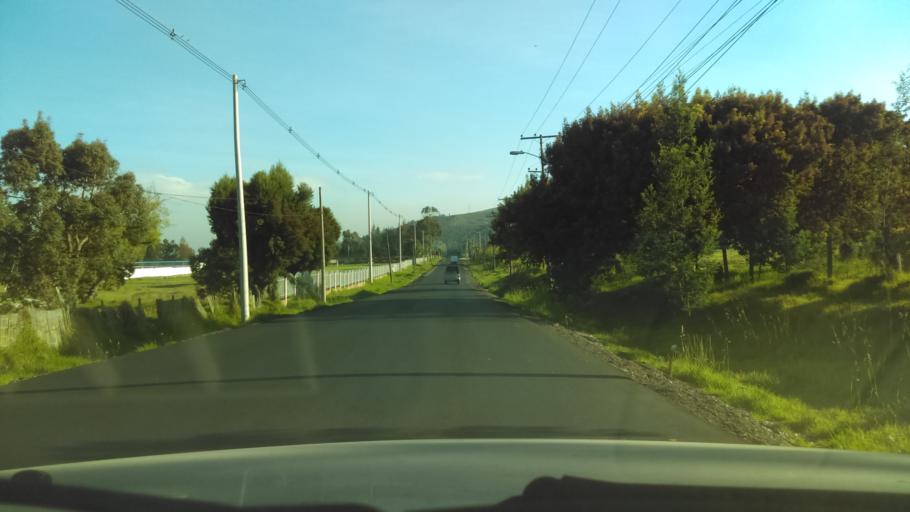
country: CO
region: Cundinamarca
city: Sibate
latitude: 4.5209
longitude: -74.2435
